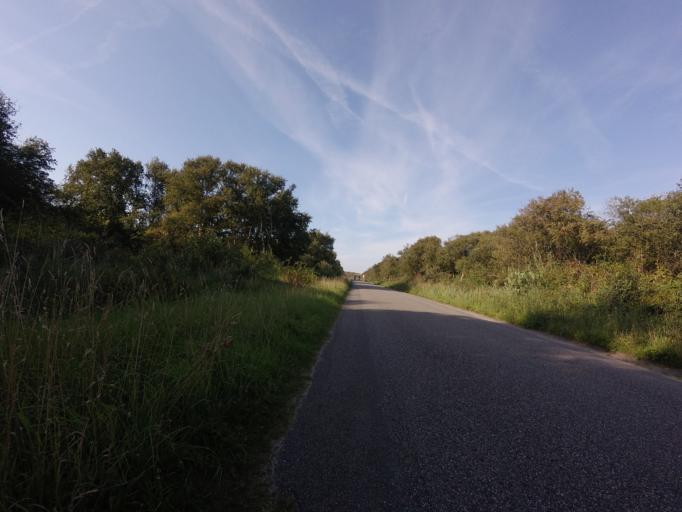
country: NL
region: Friesland
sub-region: Gemeente Schiermonnikoog
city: Schiermonnikoog
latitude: 53.4935
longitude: 6.1850
